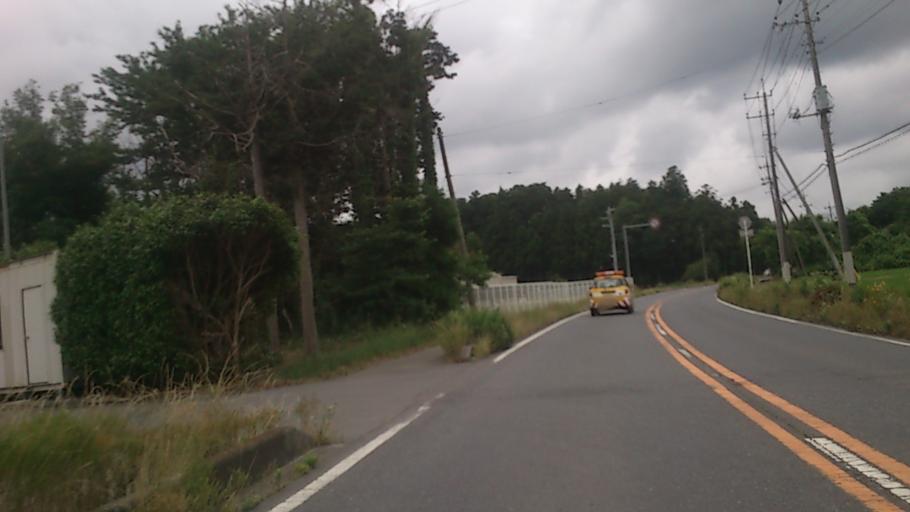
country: JP
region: Ibaraki
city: Okunoya
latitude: 36.2728
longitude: 140.3536
